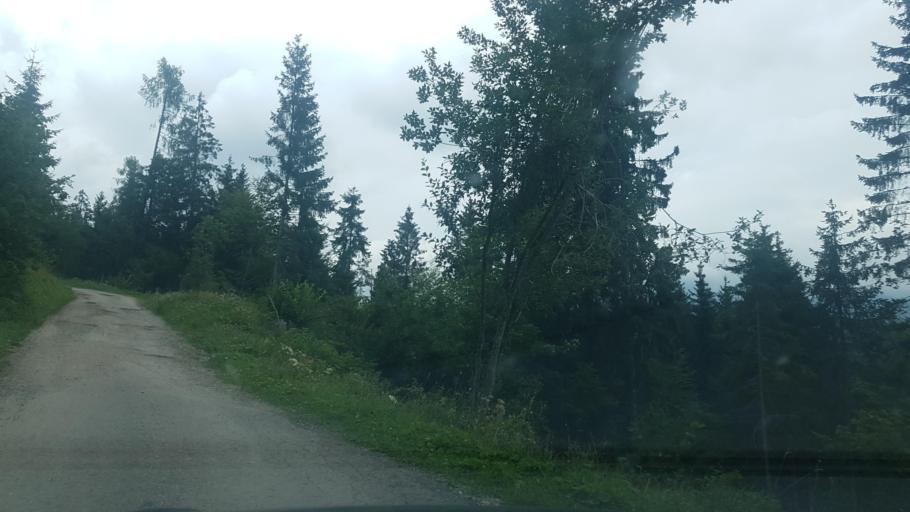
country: IT
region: Friuli Venezia Giulia
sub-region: Provincia di Udine
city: Rigolato
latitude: 46.5516
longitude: 12.8207
